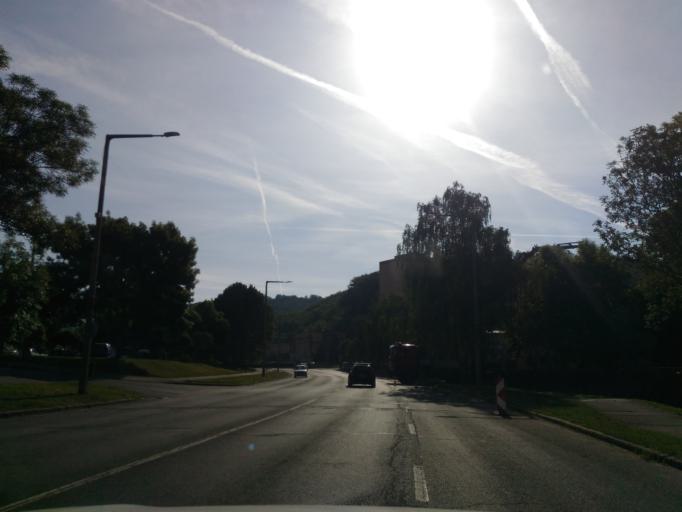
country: HU
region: Baranya
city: Komlo
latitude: 46.1895
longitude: 18.2678
